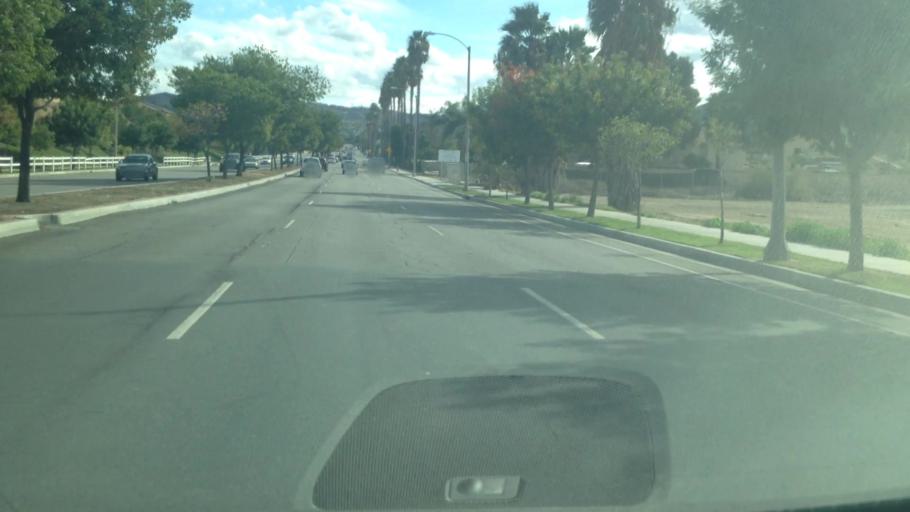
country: US
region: California
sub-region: Riverside County
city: Home Gardens
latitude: 33.8948
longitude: -117.4692
